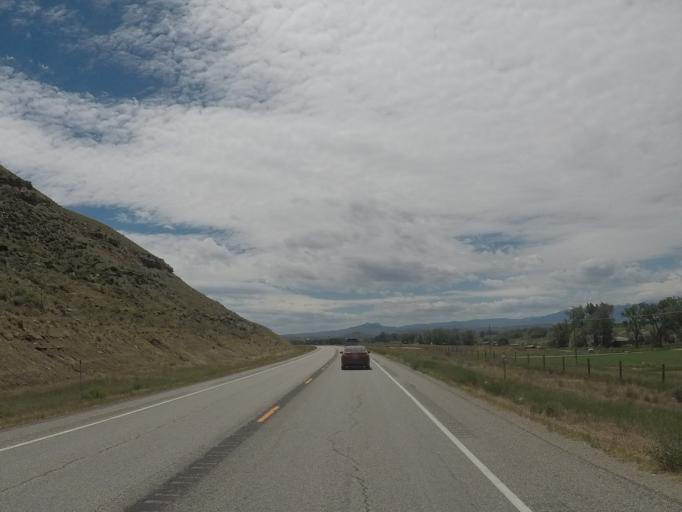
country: US
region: Montana
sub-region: Carbon County
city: Red Lodge
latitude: 45.0335
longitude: -109.0562
